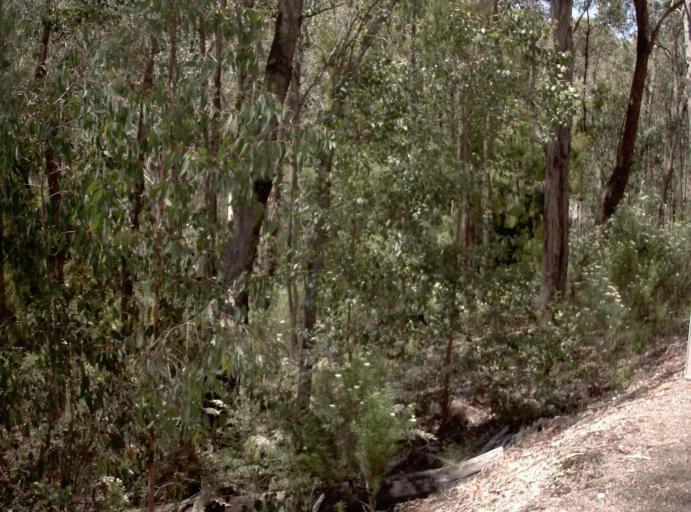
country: AU
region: Victoria
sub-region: East Gippsland
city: Lakes Entrance
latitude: -37.5790
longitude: 147.8947
